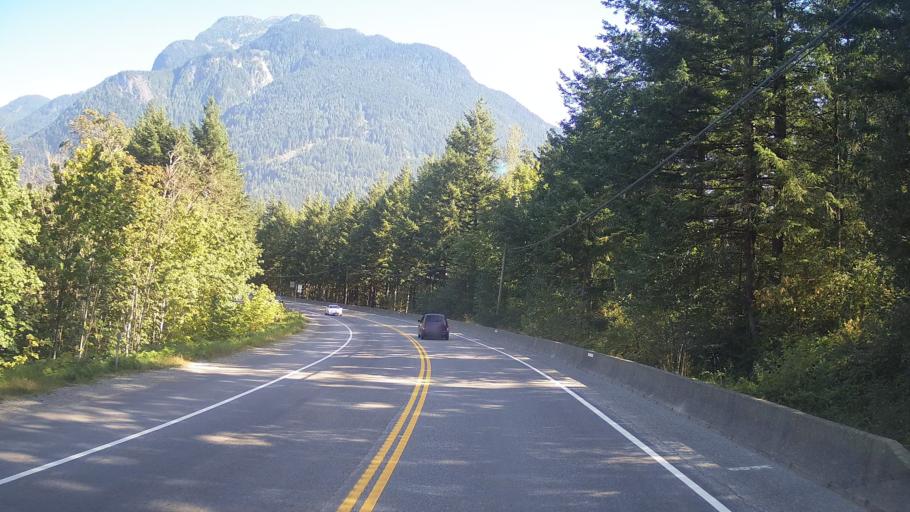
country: CA
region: British Columbia
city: Hope
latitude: 49.3880
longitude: -121.4611
